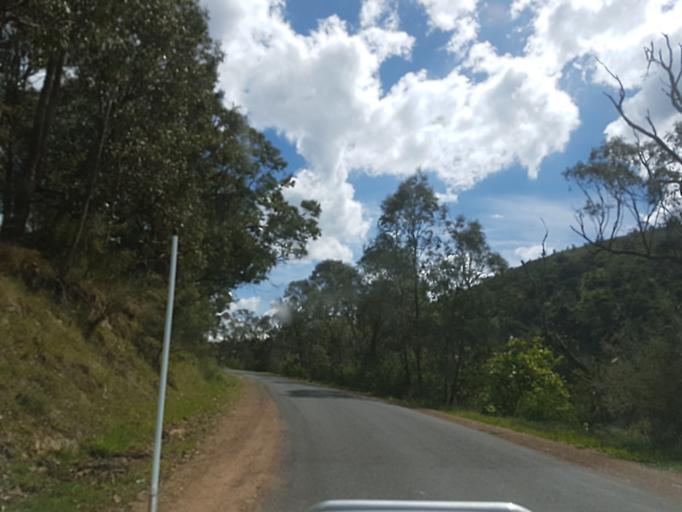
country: AU
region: Victoria
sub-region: East Gippsland
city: Bairnsdale
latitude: -37.4358
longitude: 147.2534
